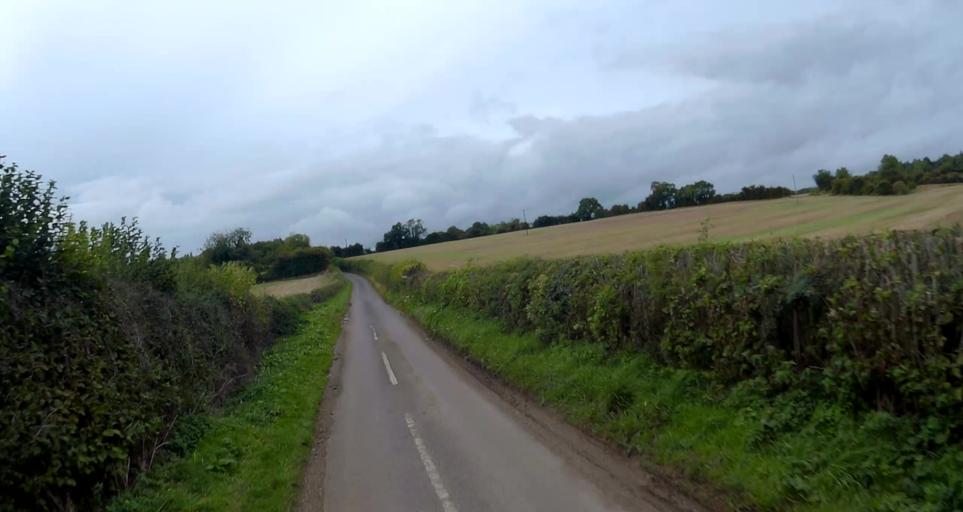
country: GB
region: England
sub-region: Hampshire
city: Four Marks
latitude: 51.1541
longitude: -1.0841
